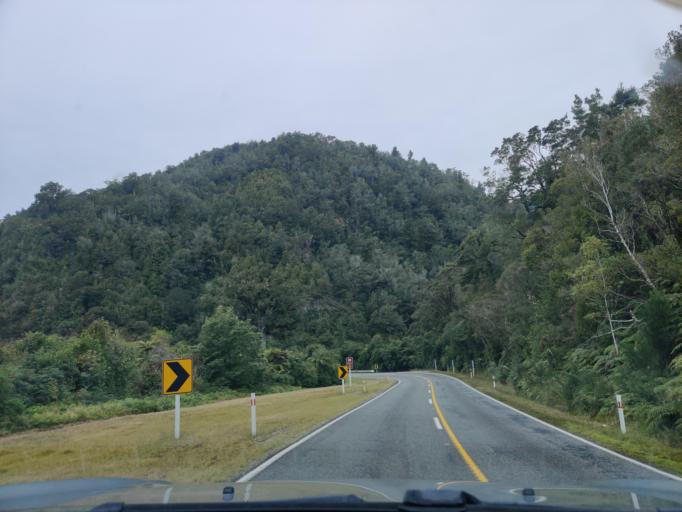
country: NZ
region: West Coast
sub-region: Buller District
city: Westport
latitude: -41.8493
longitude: 171.7297
